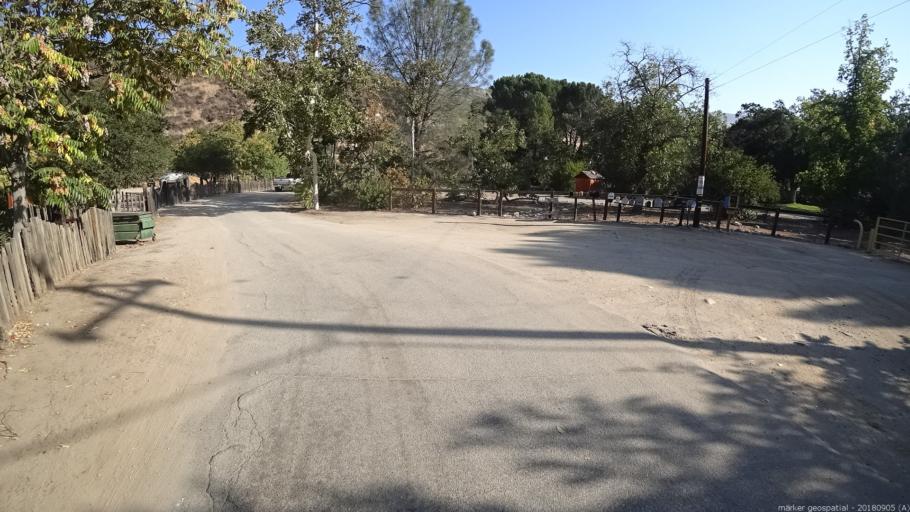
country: US
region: California
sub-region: Monterey County
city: Greenfield
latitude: 36.2647
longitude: -121.3928
